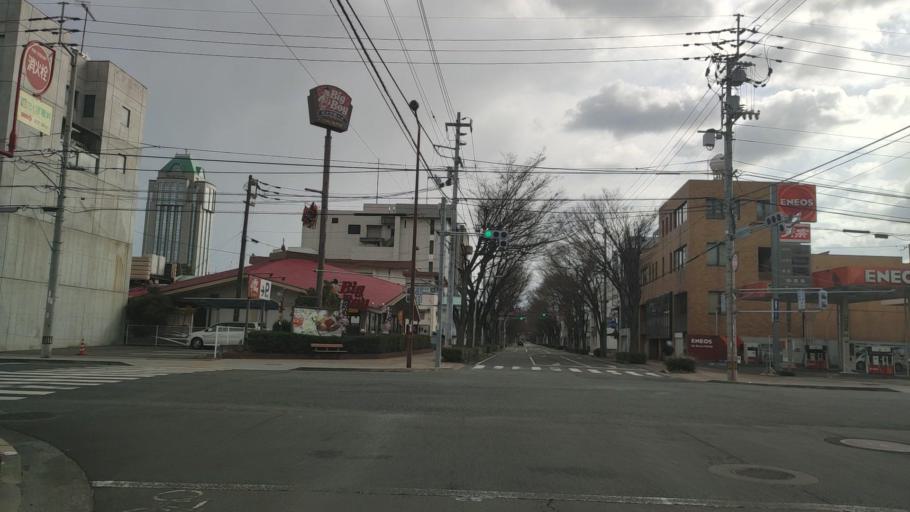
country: JP
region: Ehime
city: Hojo
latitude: 34.0632
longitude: 132.9964
